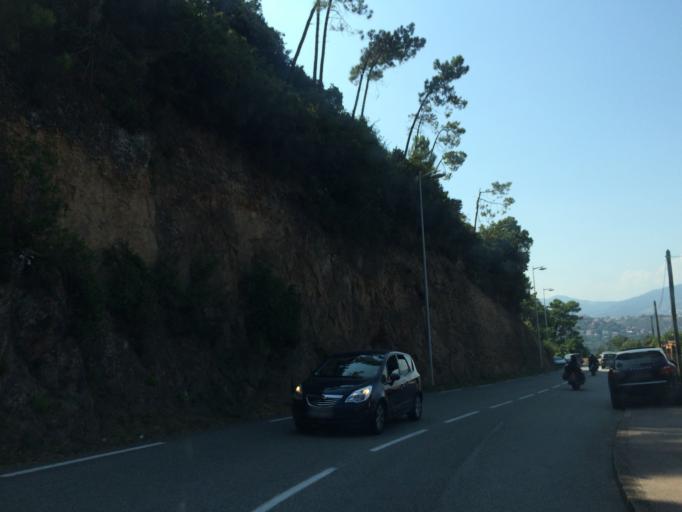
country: FR
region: Provence-Alpes-Cote d'Azur
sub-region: Departement des Alpes-Maritimes
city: Theoule-sur-Mer
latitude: 43.5046
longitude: 6.9489
